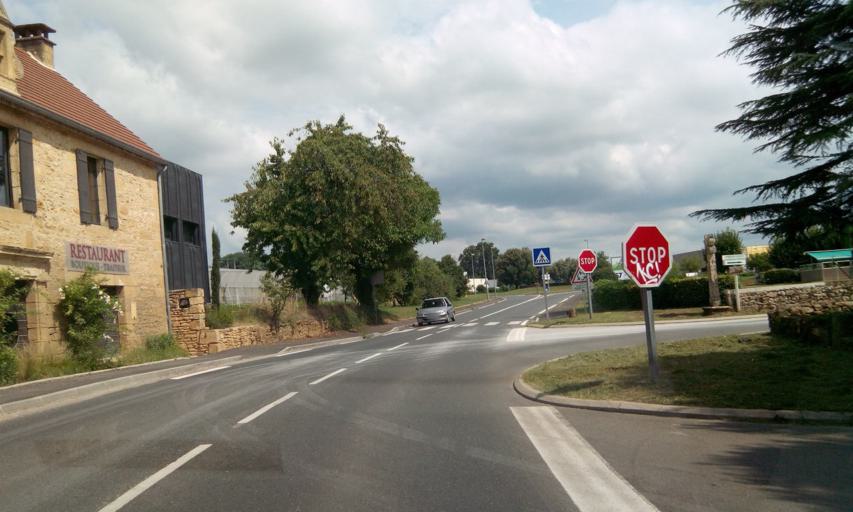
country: FR
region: Aquitaine
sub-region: Departement de la Dordogne
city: Carsac-Aillac
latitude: 44.8651
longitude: 1.2529
